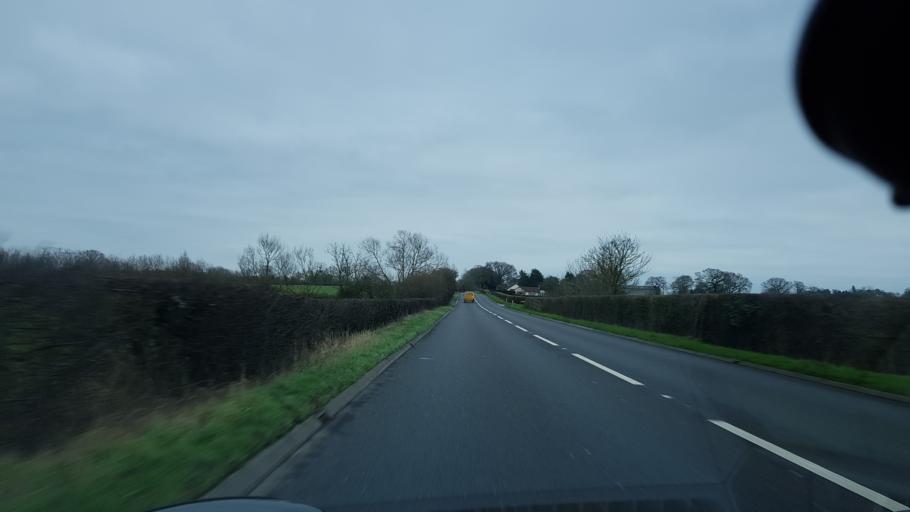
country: GB
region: England
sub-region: Somerset
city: Creech Saint Michael
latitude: 50.9611
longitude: -2.9878
